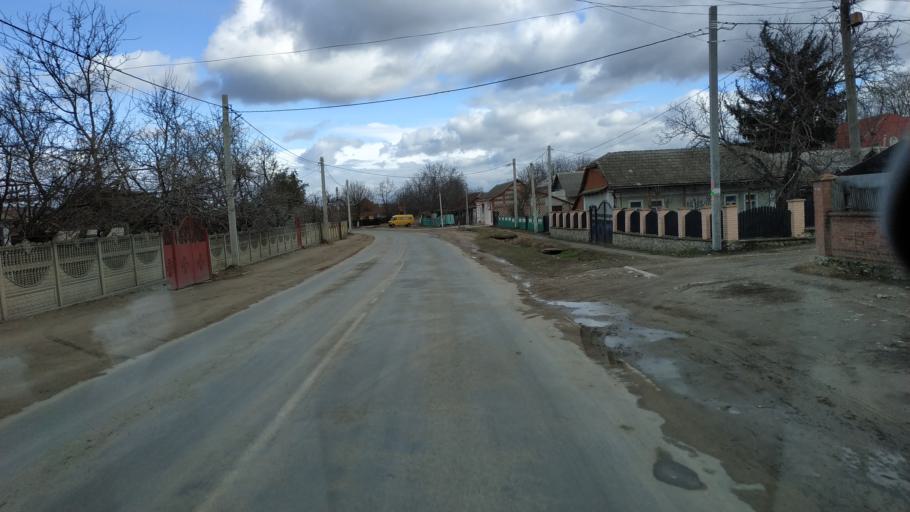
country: MD
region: Stinga Nistrului
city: Bucovat
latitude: 47.1559
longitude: 28.4302
